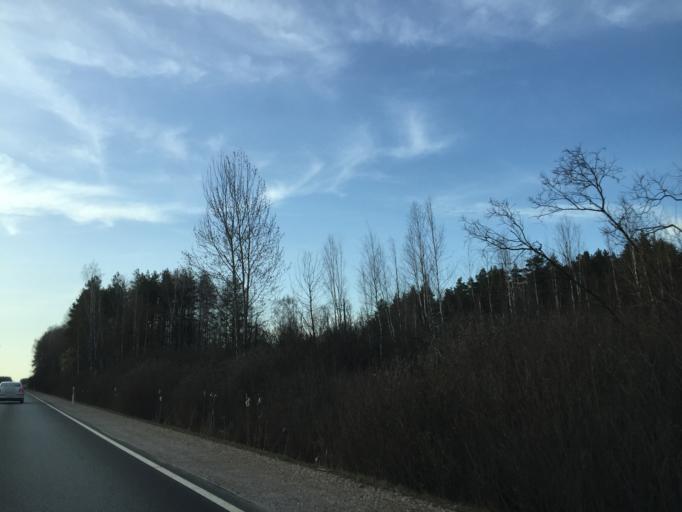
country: LV
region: Ikskile
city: Ikskile
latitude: 56.8793
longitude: 24.5159
